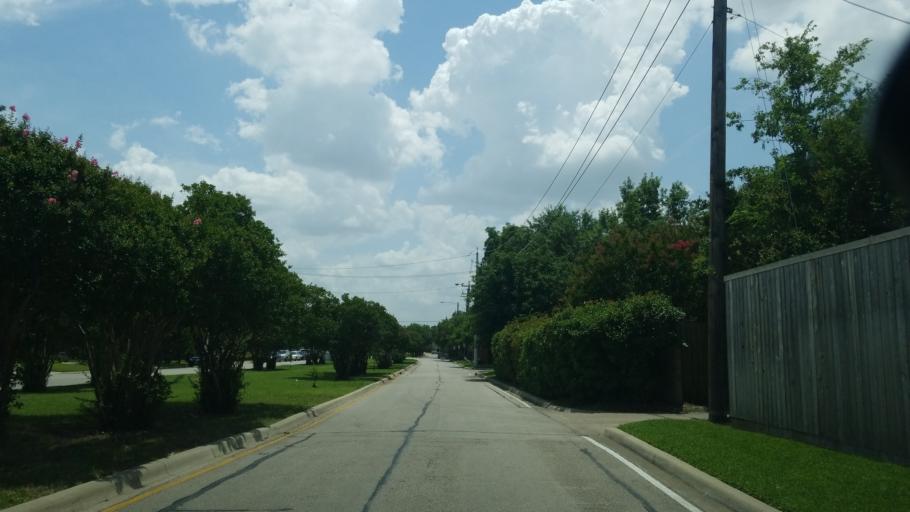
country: US
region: Texas
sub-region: Dallas County
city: University Park
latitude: 32.8691
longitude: -96.7955
